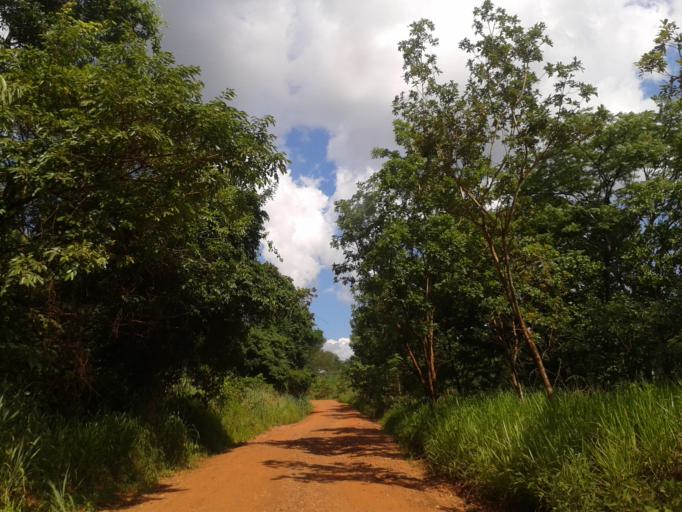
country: BR
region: Minas Gerais
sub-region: Campina Verde
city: Campina Verde
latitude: -19.3173
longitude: -49.8145
